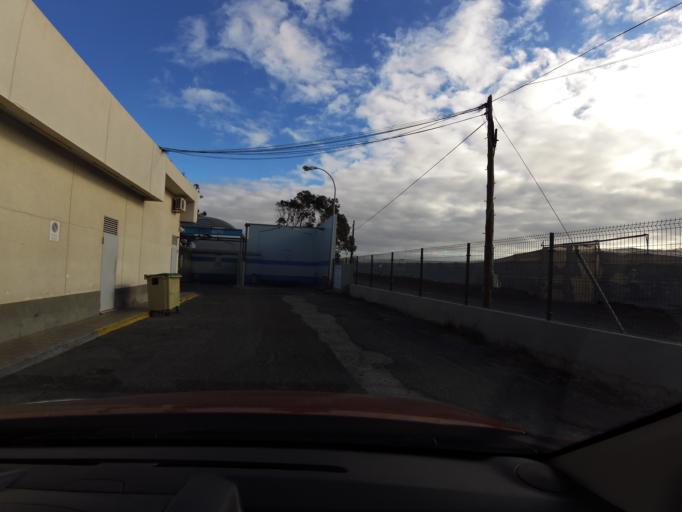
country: ES
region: Canary Islands
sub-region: Provincia de Las Palmas
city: Cruce de Arinaga
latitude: 27.8038
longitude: -15.4822
